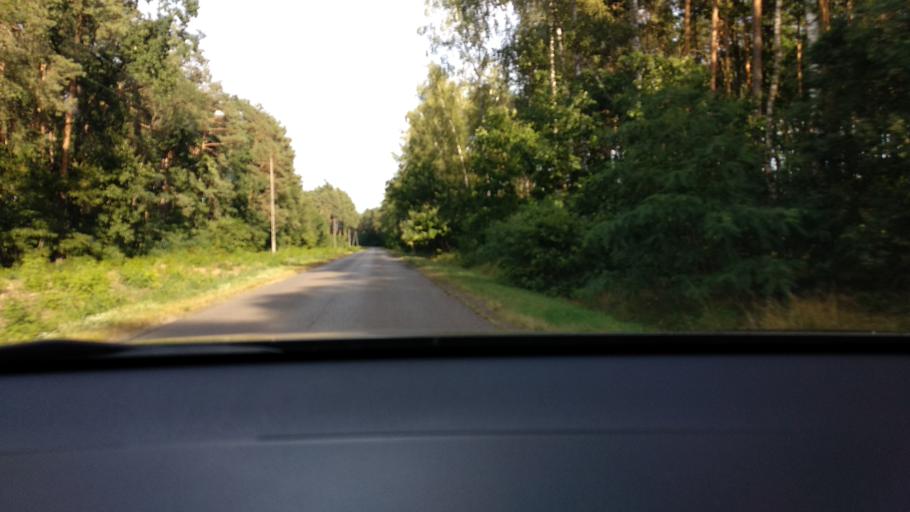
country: PL
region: Masovian Voivodeship
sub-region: Powiat pultuski
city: Pultusk
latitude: 52.7130
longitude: 21.1540
